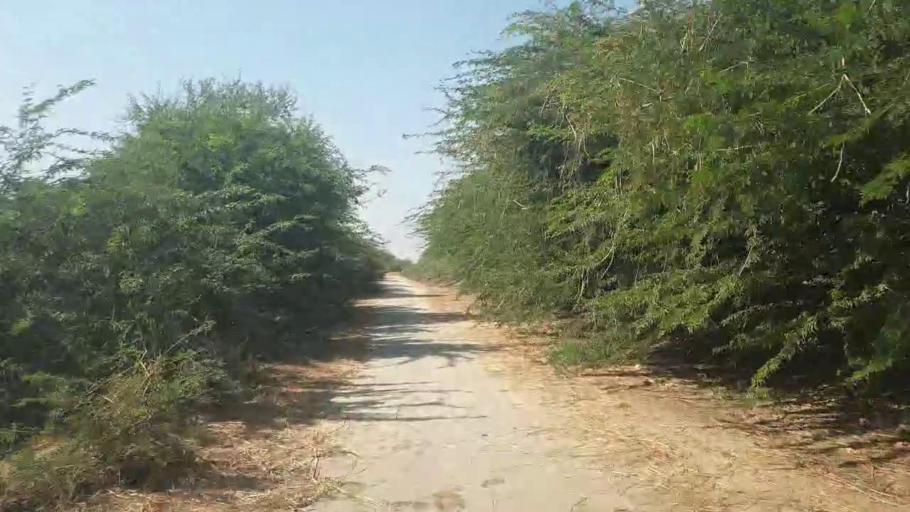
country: PK
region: Sindh
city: Badin
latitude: 24.6460
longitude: 68.9139
